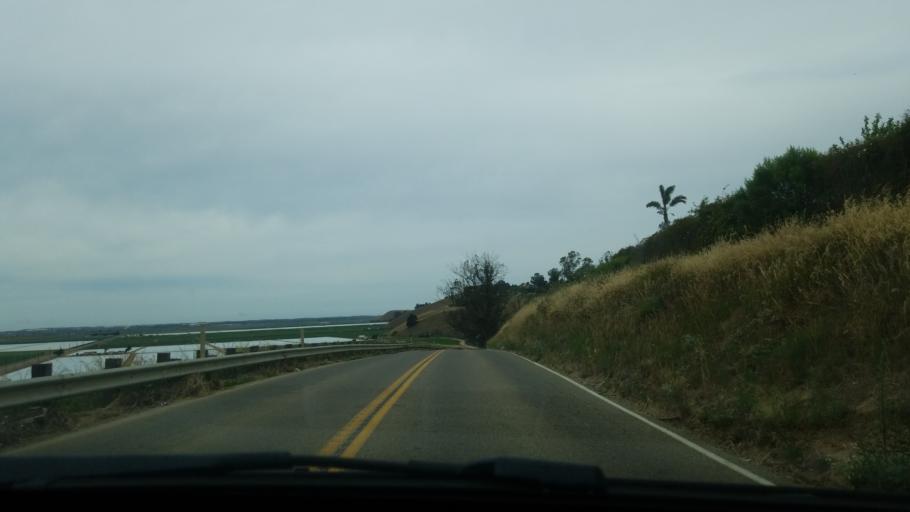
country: US
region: California
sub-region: San Luis Obispo County
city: Nipomo
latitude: 35.0089
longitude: -120.4967
